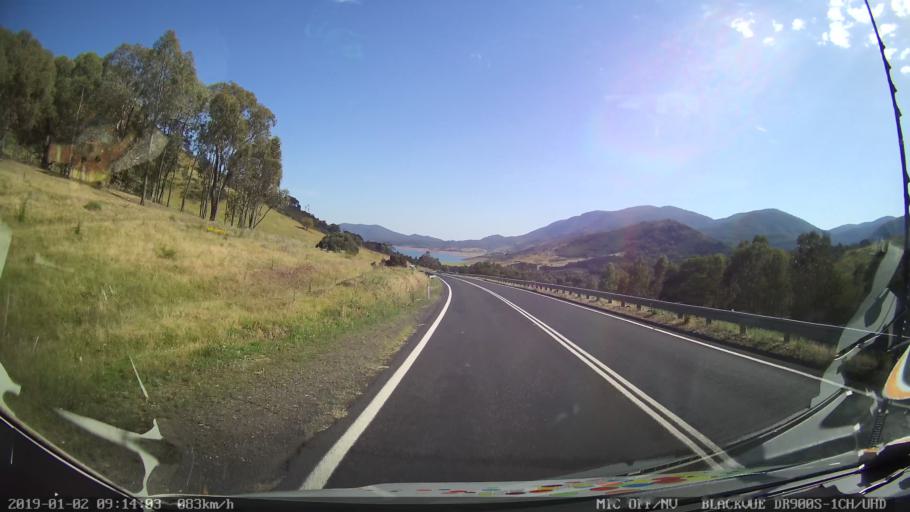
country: AU
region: New South Wales
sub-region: Tumut Shire
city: Tumut
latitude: -35.4822
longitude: 148.2722
